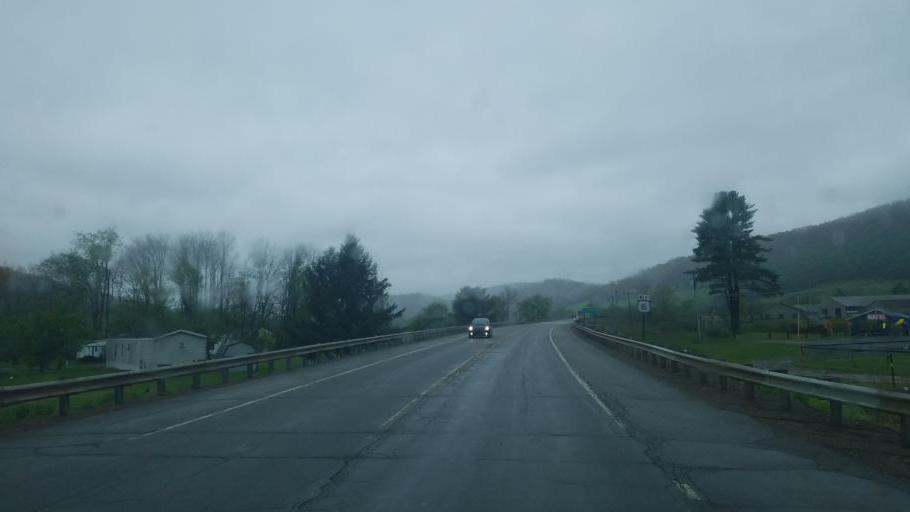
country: US
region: Pennsylvania
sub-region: McKean County
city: Port Allegany
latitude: 41.7838
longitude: -78.1611
